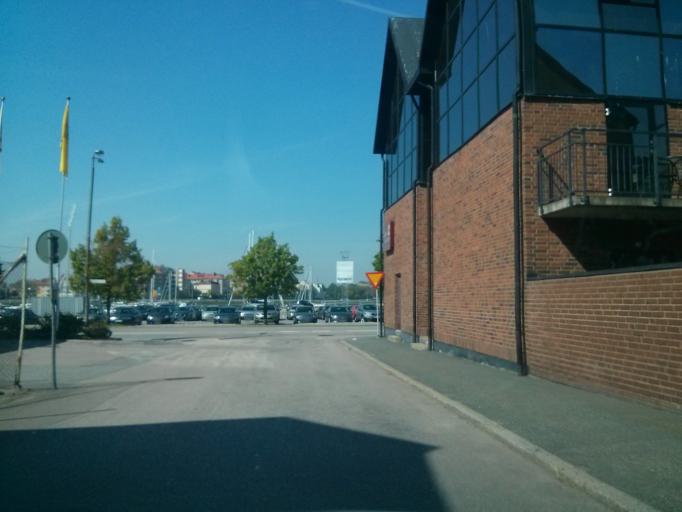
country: SE
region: Blekinge
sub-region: Karlskrona Kommun
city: Karlskrona
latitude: 56.1668
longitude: 15.5896
